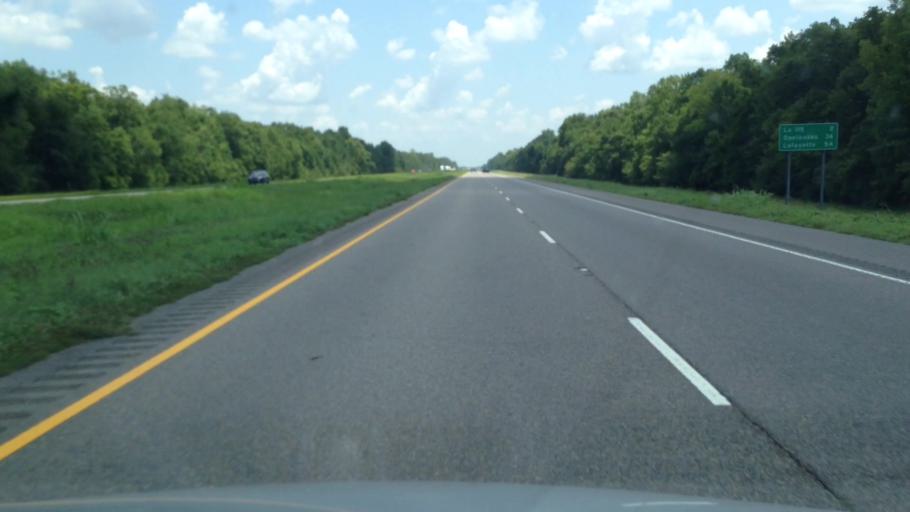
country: US
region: Louisiana
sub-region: Avoyelles Parish
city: Bunkie
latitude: 30.9769
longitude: -92.2971
